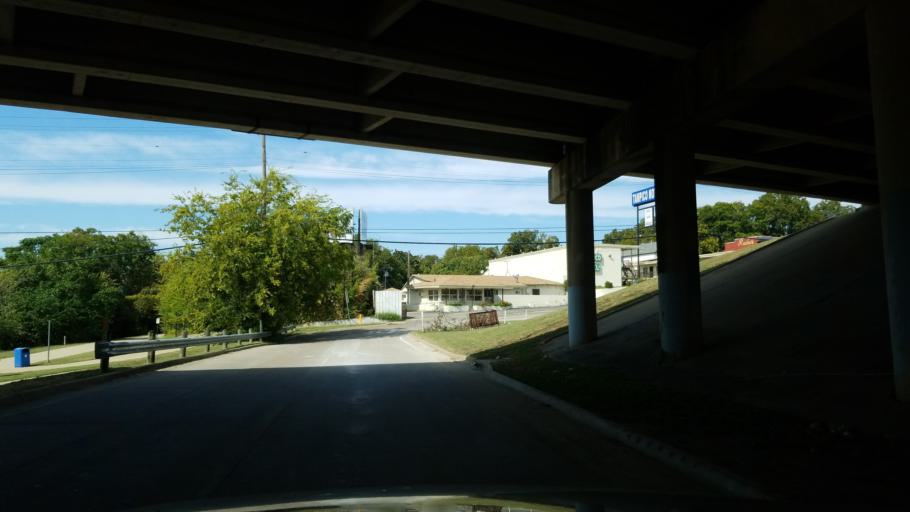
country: US
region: Texas
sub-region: Dallas County
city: Highland Park
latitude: 32.8066
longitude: -96.7330
